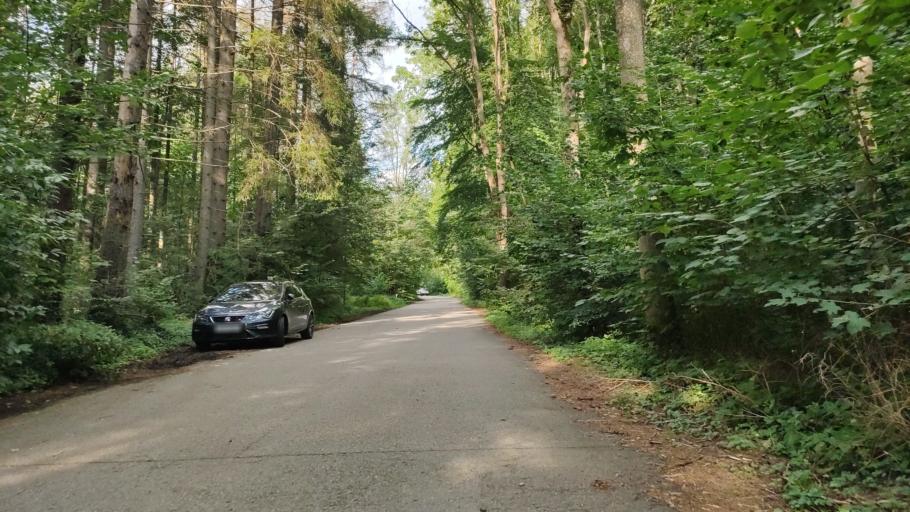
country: DE
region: Bavaria
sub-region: Upper Bavaria
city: Scheuring
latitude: 48.1481
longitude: 10.8705
